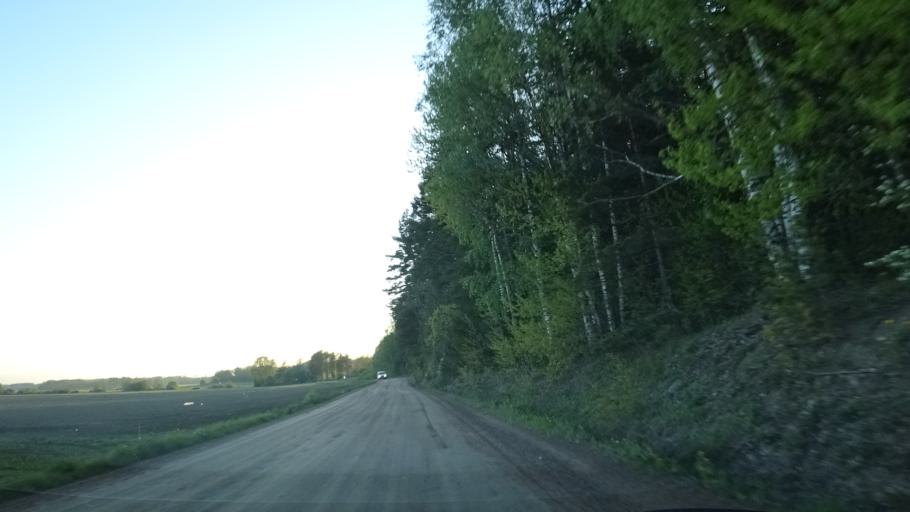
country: FI
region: Uusimaa
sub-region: Helsinki
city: Siuntio
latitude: 60.0797
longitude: 24.1900
